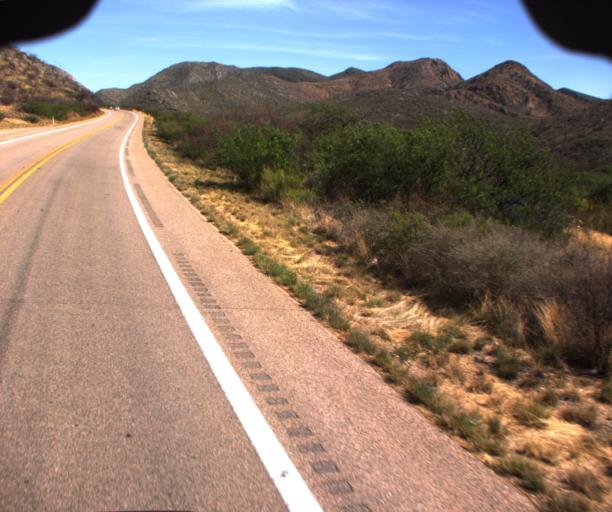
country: US
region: Arizona
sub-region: Cochise County
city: Bisbee
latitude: 31.5198
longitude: -110.0307
